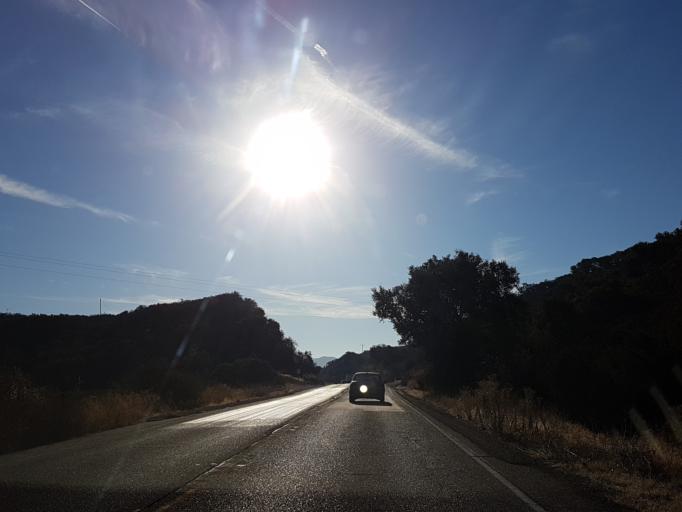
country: US
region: California
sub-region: Santa Barbara County
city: Santa Ynez
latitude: 34.5651
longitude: -119.9377
